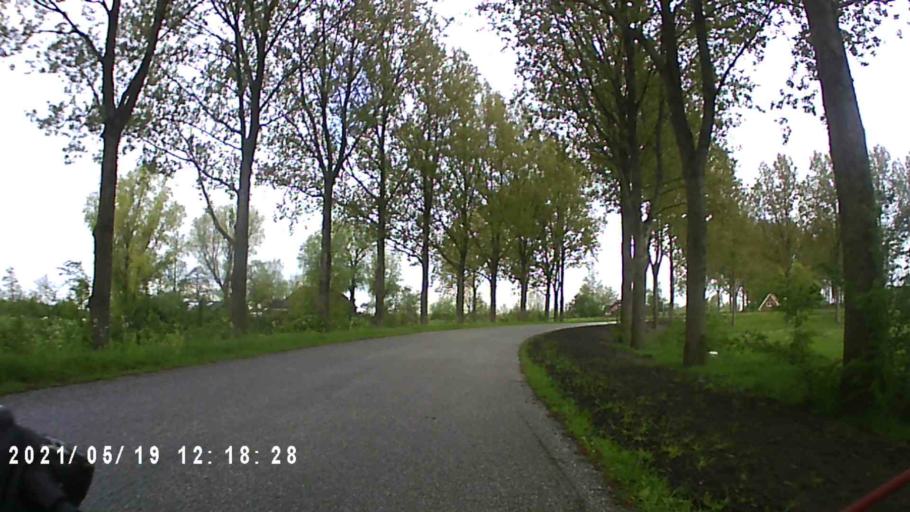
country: NL
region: Friesland
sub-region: Gemeente Kollumerland en Nieuwkruisland
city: Kollum
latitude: 53.2602
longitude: 6.1709
